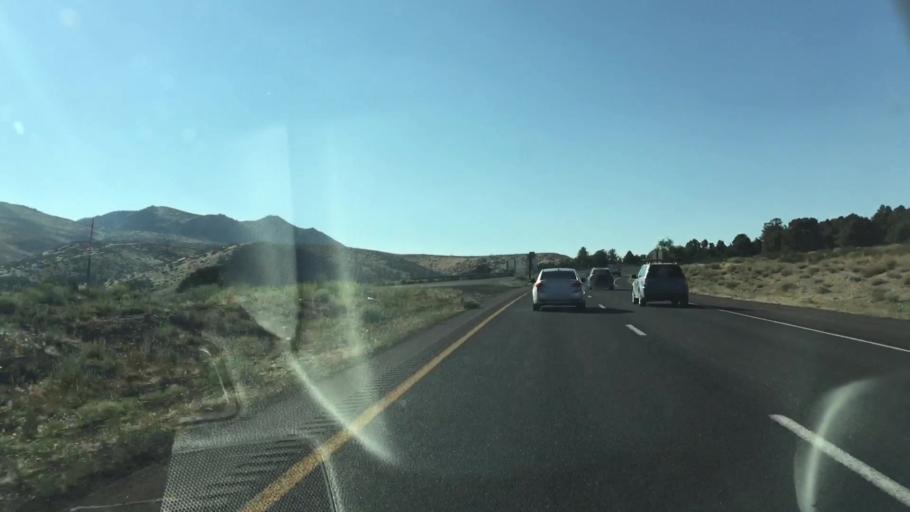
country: US
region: California
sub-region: Inyo County
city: West Bishop
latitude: 37.5345
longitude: -118.6352
